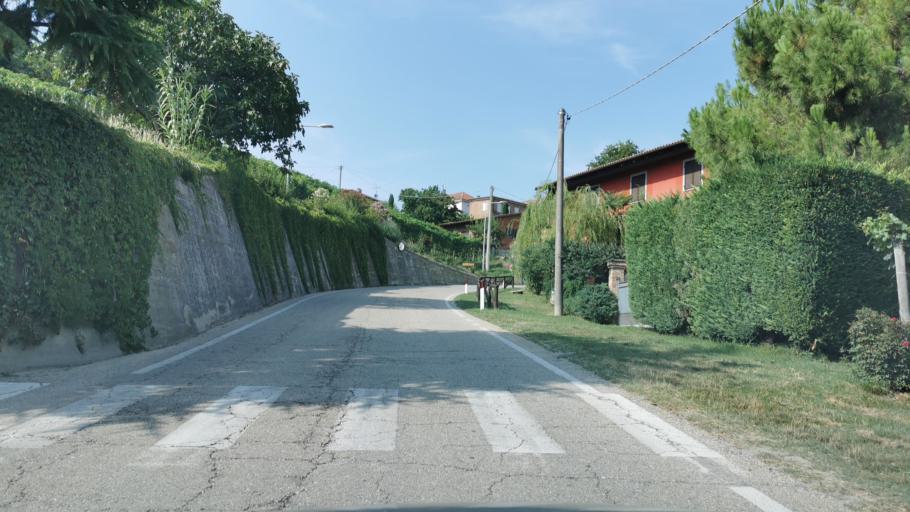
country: IT
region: Piedmont
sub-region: Provincia di Cuneo
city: La Morra
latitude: 44.6504
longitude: 7.9454
